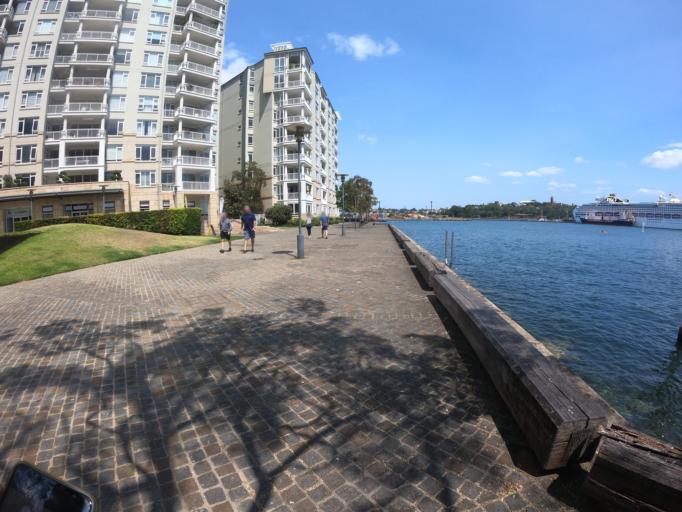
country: AU
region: New South Wales
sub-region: Leichhardt
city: Balmain East
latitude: -33.8657
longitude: 151.1909
